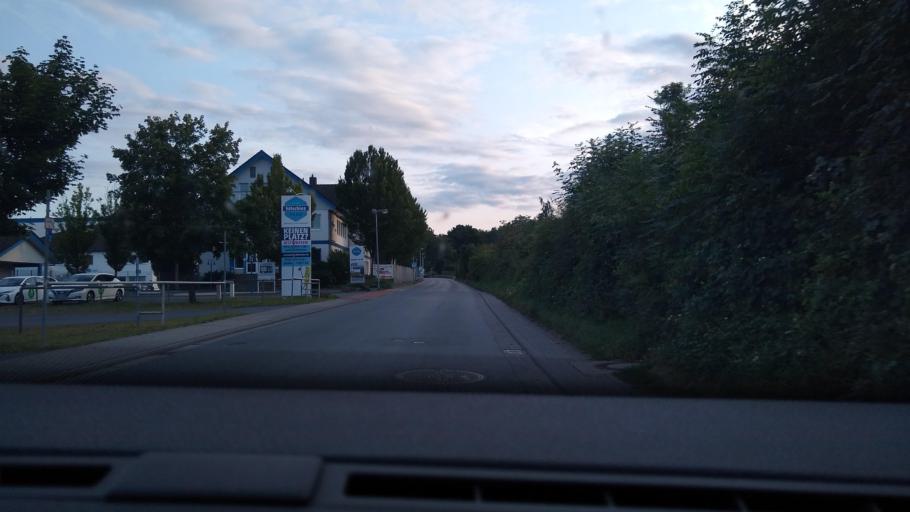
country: DE
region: Hesse
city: Michelstadt
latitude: 49.6770
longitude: 8.9942
